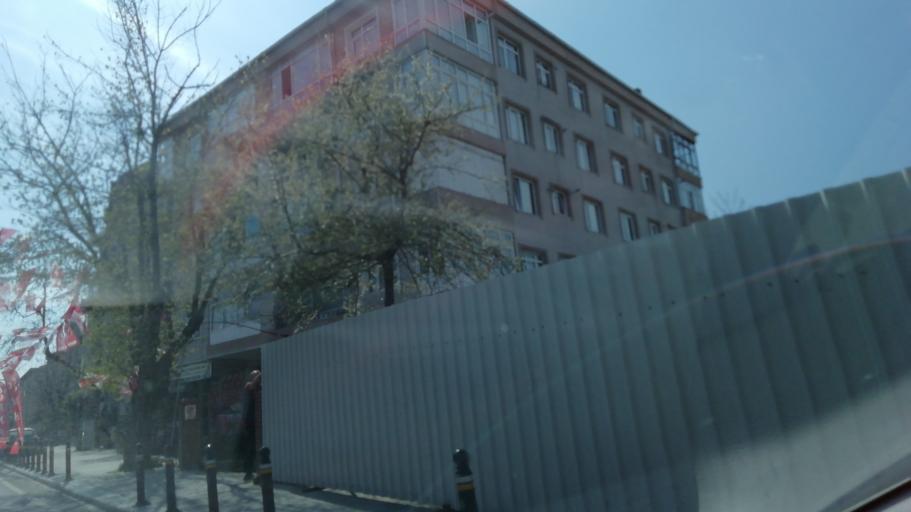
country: TR
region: Istanbul
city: Mahmutbey
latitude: 41.0002
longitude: 28.7711
